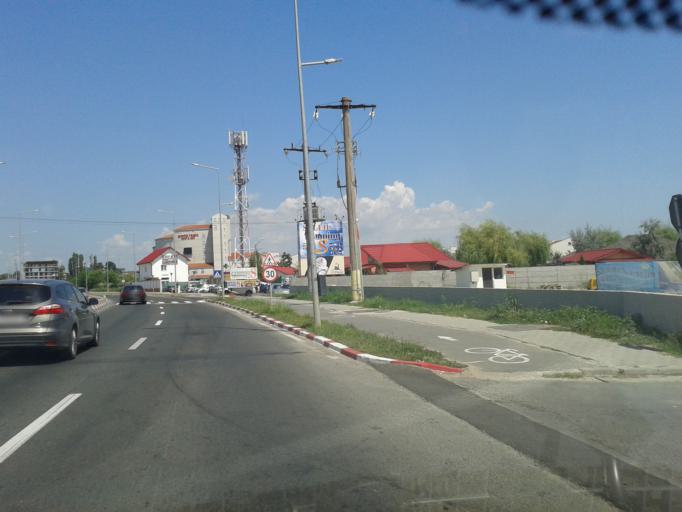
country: RO
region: Constanta
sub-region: Comuna Navodari
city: Navodari
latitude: 44.2836
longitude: 28.6185
